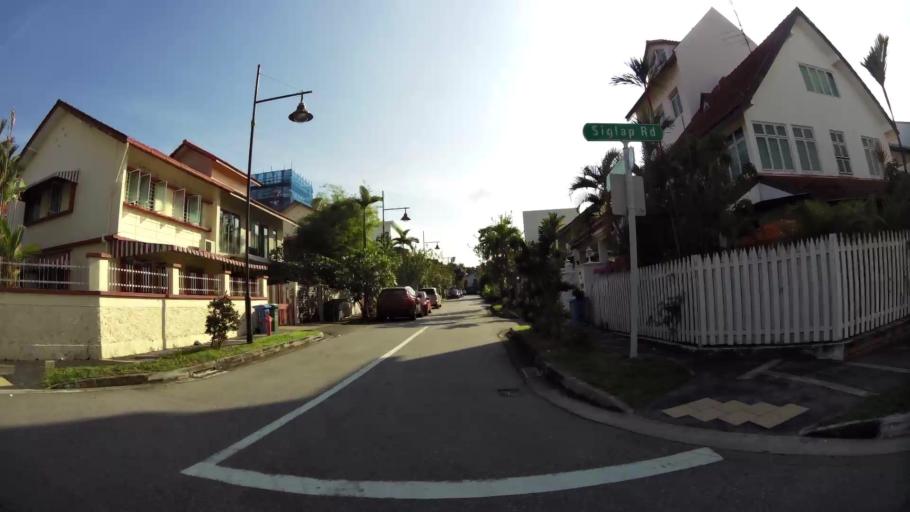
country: SG
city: Singapore
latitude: 1.3152
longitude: 103.9227
